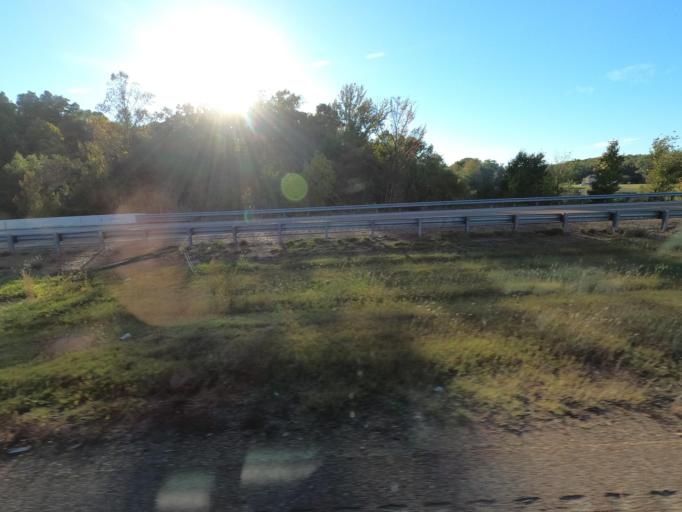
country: US
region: Tennessee
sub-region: Fayette County
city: Hickory Withe
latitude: 35.1981
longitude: -89.6521
